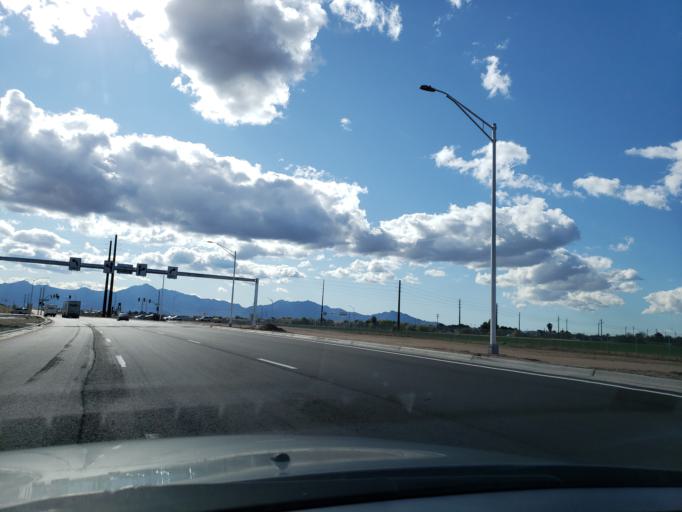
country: US
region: Arizona
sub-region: Maricopa County
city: Laveen
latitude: 33.4242
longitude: -112.1900
